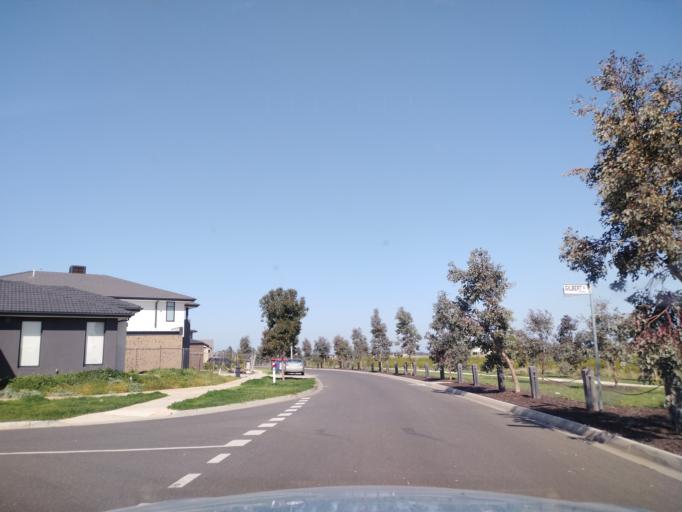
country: AU
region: Victoria
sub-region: Wyndham
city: Williams Landing
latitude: -37.8452
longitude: 144.7344
